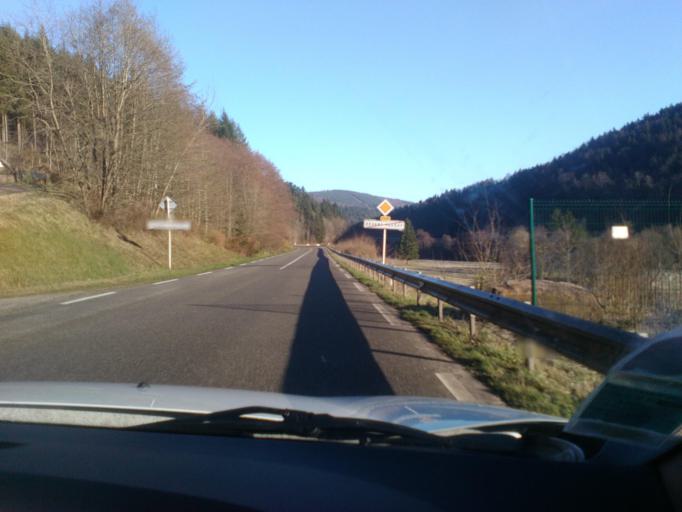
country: FR
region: Alsace
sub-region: Departement du Bas-Rhin
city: Rothau
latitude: 48.4253
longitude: 7.1841
